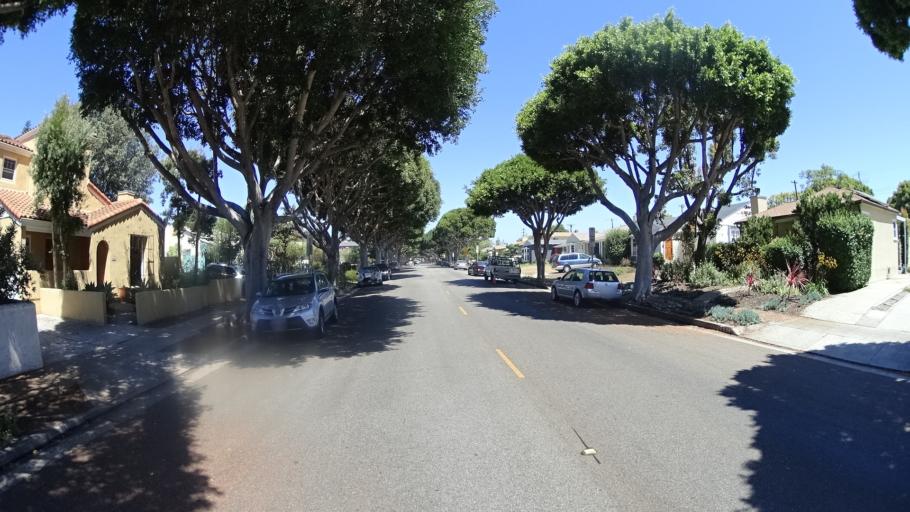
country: US
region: California
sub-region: Los Angeles County
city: Santa Monica
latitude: 34.0176
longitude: -118.4623
